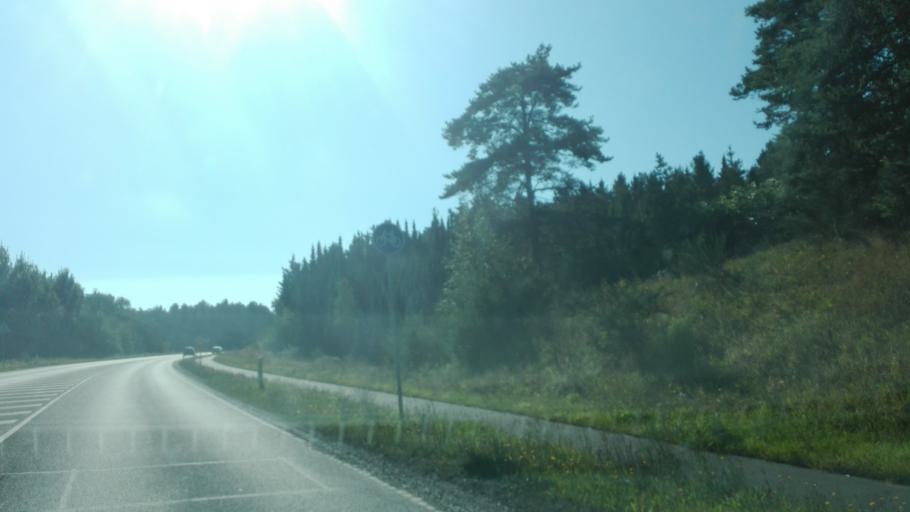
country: DK
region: Central Jutland
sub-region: Syddjurs Kommune
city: Ebeltoft
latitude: 56.2410
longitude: 10.6558
